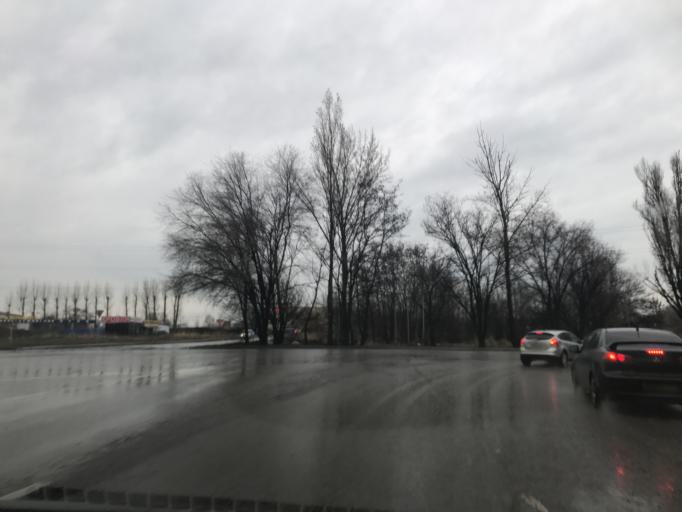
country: RU
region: Rostov
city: Severnyy
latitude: 47.2999
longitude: 39.7123
